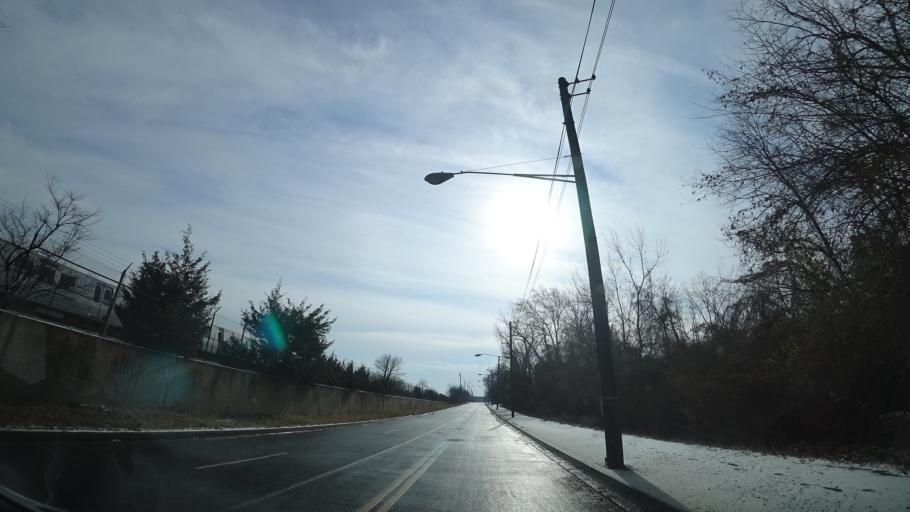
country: US
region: Maryland
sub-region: Prince George's County
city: Chillum
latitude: 38.9458
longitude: -76.9999
